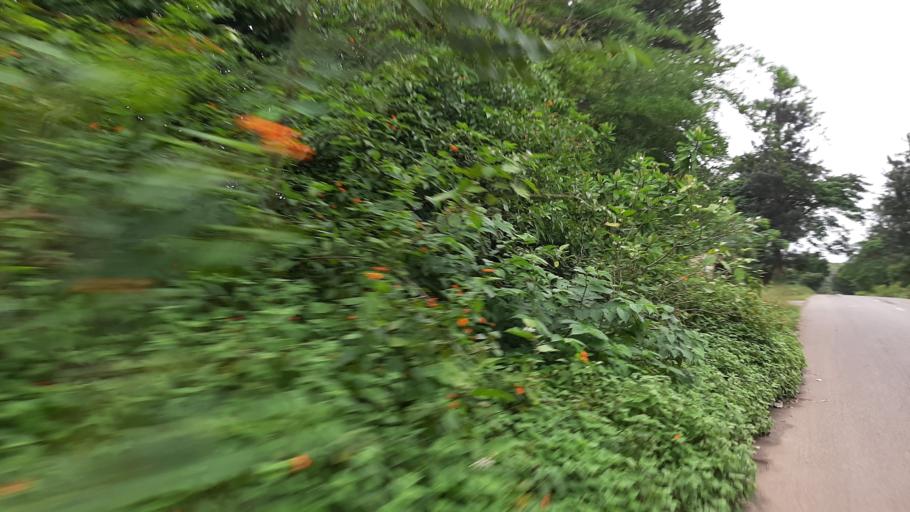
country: IN
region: Andhra Pradesh
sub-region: Vizianagaram District
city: Salur
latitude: 18.3008
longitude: 82.9110
